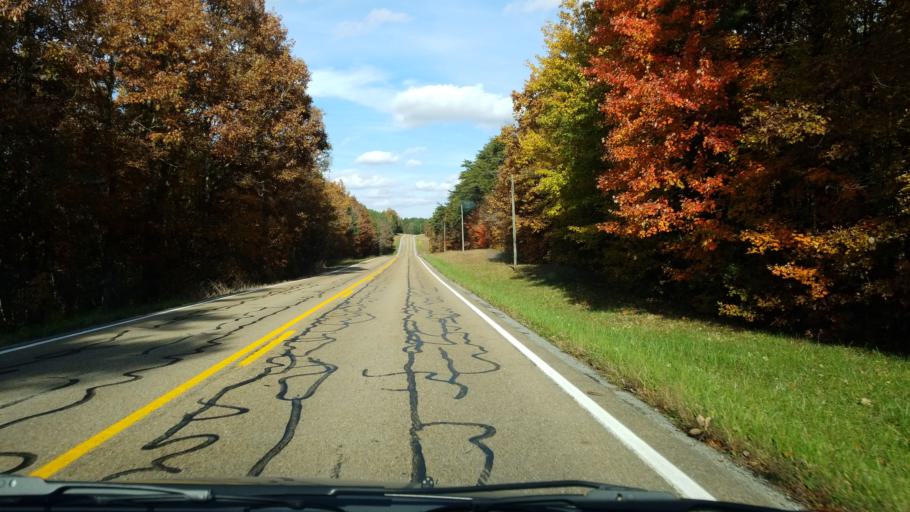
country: US
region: Tennessee
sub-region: Sequatchie County
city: Dunlap
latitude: 35.4527
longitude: -85.5007
